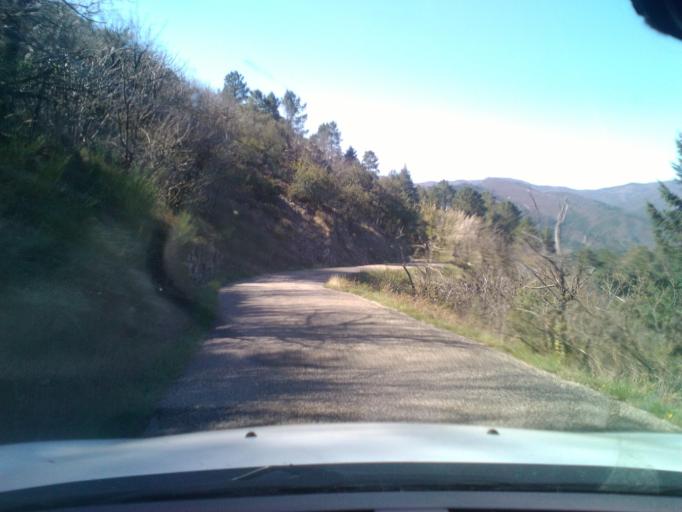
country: FR
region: Languedoc-Roussillon
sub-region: Departement du Gard
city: Saint-Jean-du-Gard
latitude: 44.1412
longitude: 3.7714
